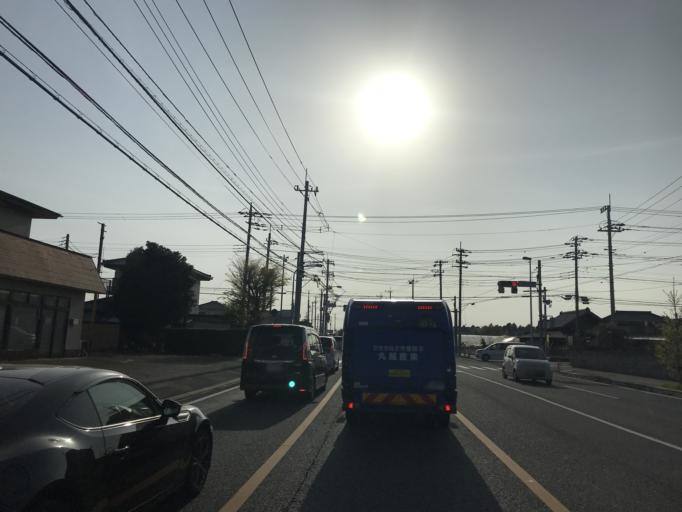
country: JP
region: Ibaraki
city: Hitachi-Naka
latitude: 36.4009
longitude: 140.5760
